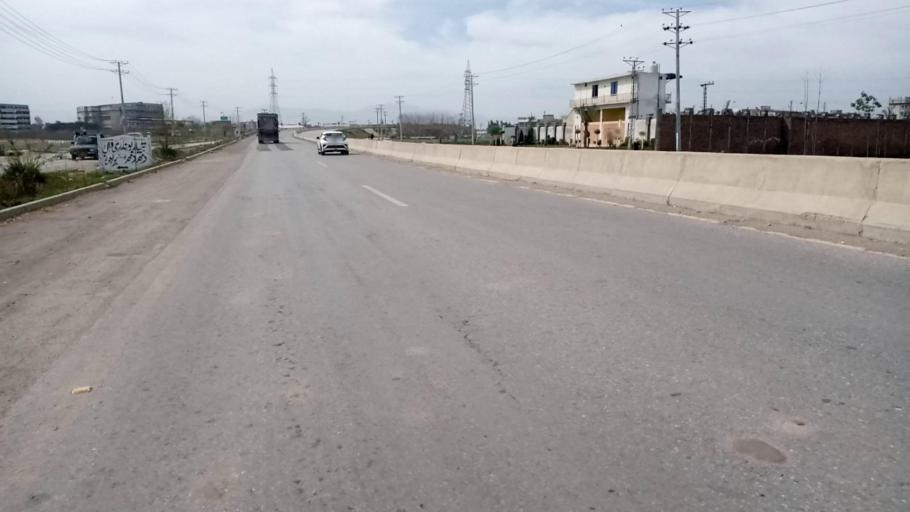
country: PK
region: Khyber Pakhtunkhwa
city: Peshawar
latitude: 34.0380
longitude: 71.6255
